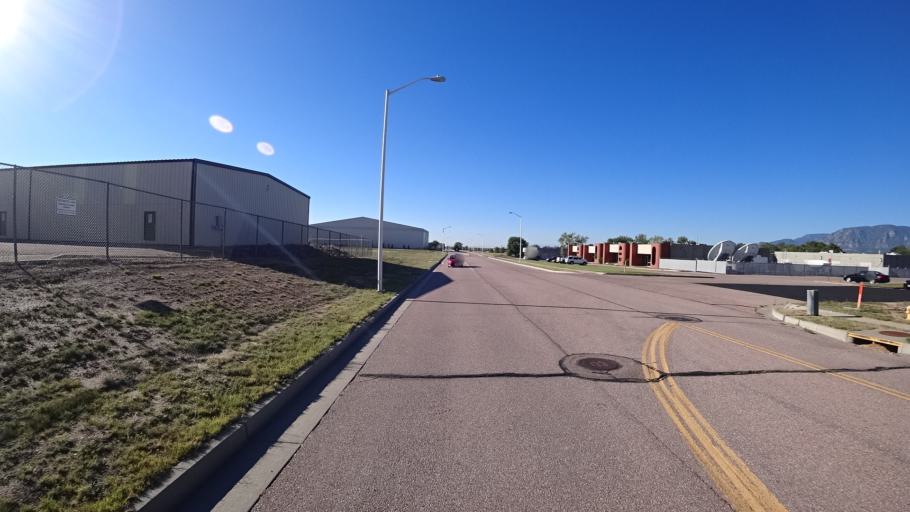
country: US
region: Colorado
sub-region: El Paso County
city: Cimarron Hills
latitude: 38.8103
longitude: -104.7237
